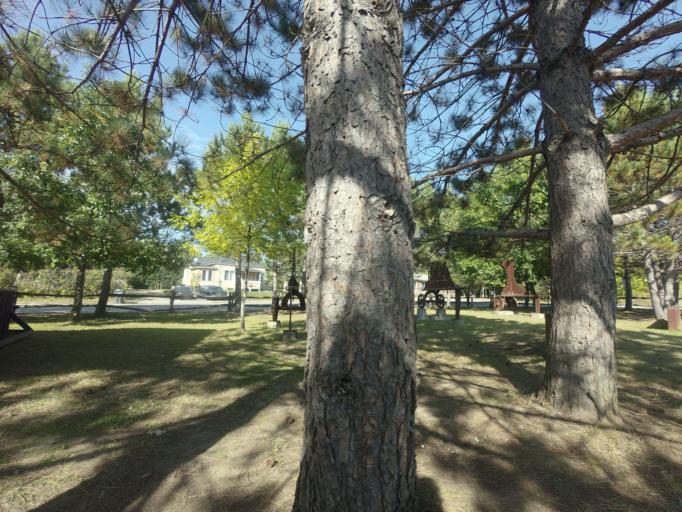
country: CA
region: Quebec
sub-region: Laurentides
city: Labelle
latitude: 46.2841
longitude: -74.7344
